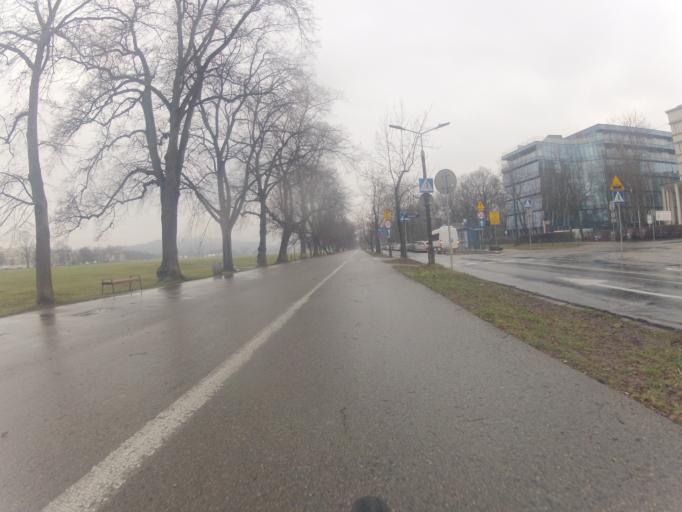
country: PL
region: Lesser Poland Voivodeship
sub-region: Krakow
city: Krakow
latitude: 50.0596
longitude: 19.9210
